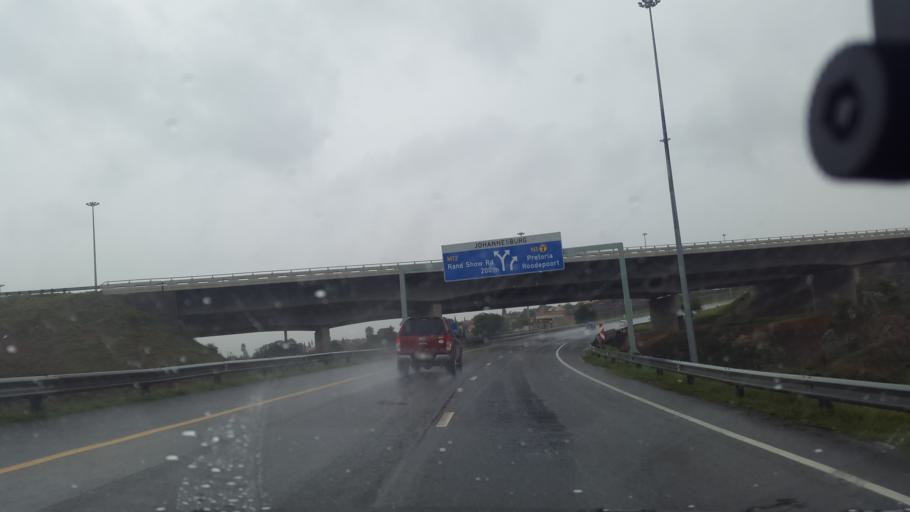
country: ZA
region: Gauteng
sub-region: City of Johannesburg Metropolitan Municipality
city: Johannesburg
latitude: -26.2593
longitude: 27.9628
